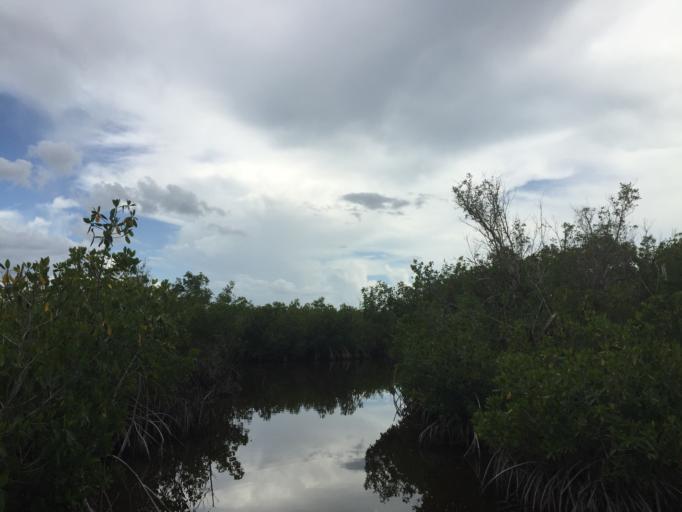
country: US
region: Florida
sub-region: Collier County
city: Marco
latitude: 25.9004
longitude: -81.3738
